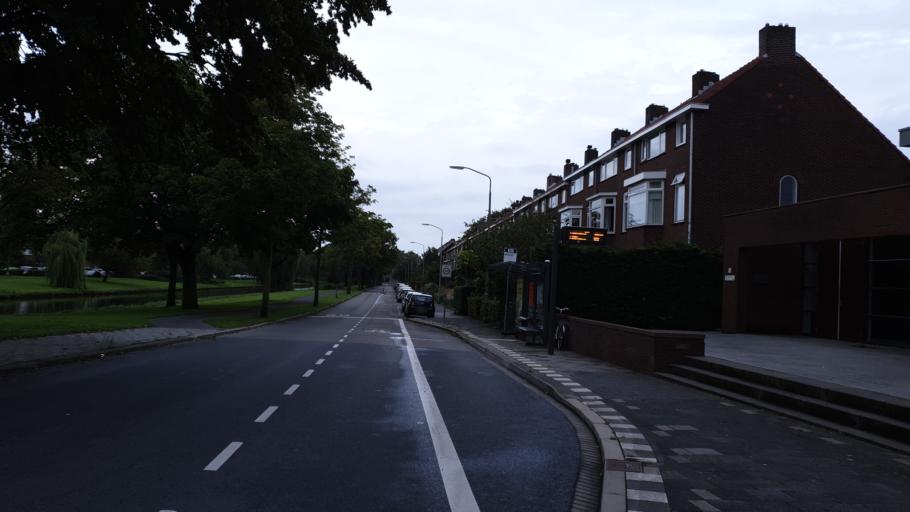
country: NL
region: South Holland
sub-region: Gemeente Dordrecht
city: Dordrecht
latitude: 51.8049
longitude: 4.6569
